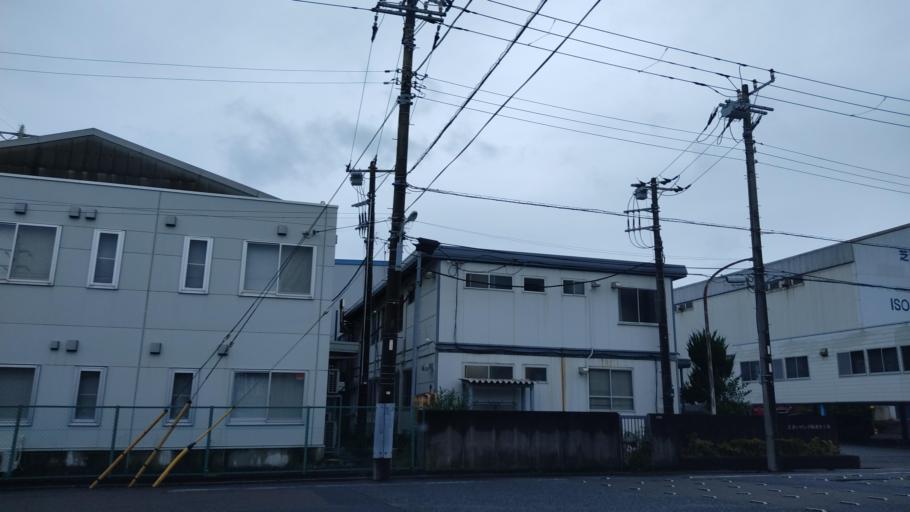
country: JP
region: Tokyo
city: Urayasu
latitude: 35.6327
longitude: 139.9001
